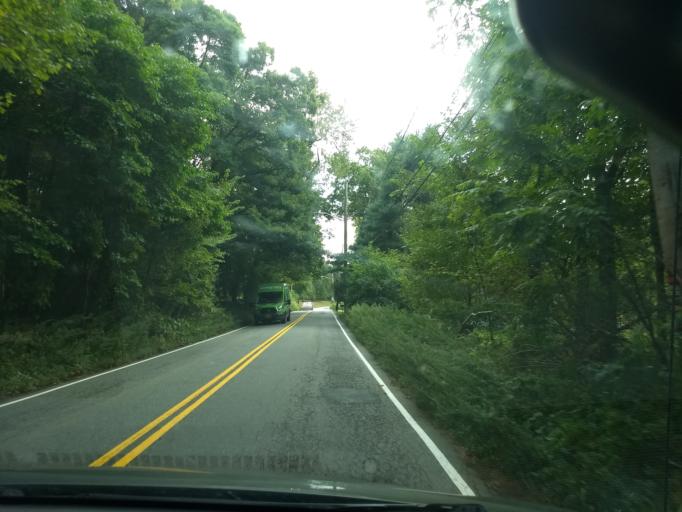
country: US
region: New York
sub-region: Rockland County
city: Spring Valley
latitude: 41.0996
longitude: -74.0427
